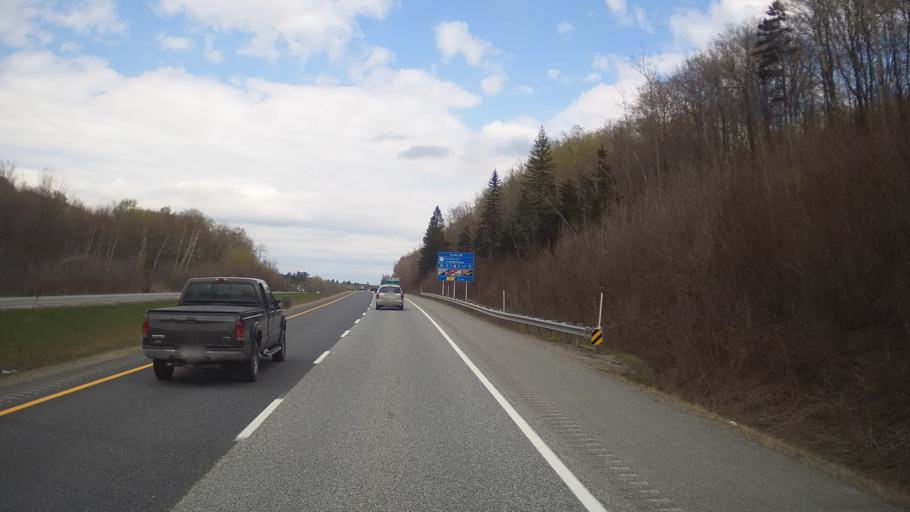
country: CA
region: Quebec
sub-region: Estrie
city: Magog
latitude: 45.2896
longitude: -72.2481
